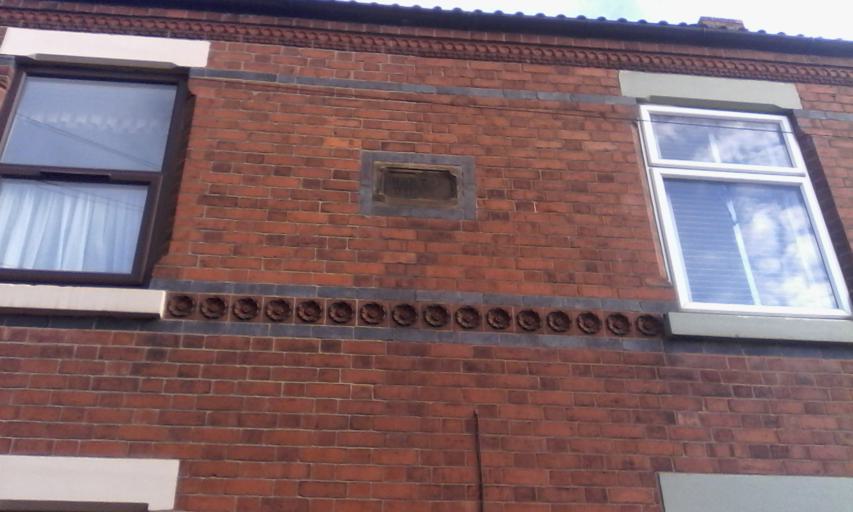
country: GB
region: England
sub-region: Nottinghamshire
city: Arnold
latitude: 52.9807
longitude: -1.1184
